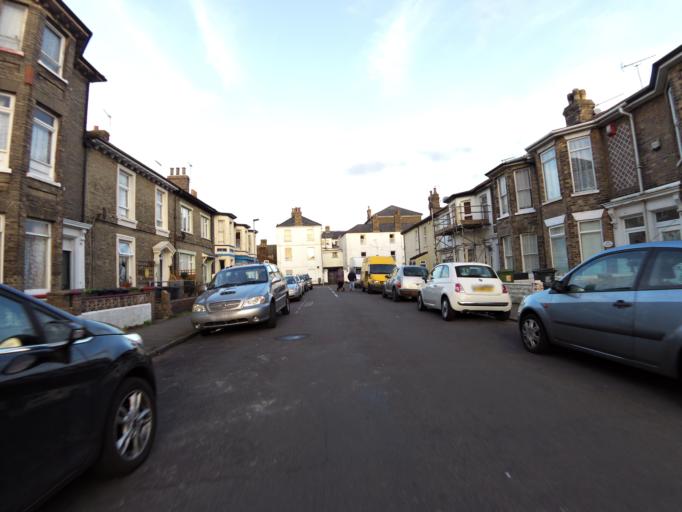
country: GB
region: England
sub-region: Norfolk
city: Great Yarmouth
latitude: 52.6013
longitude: 1.7344
